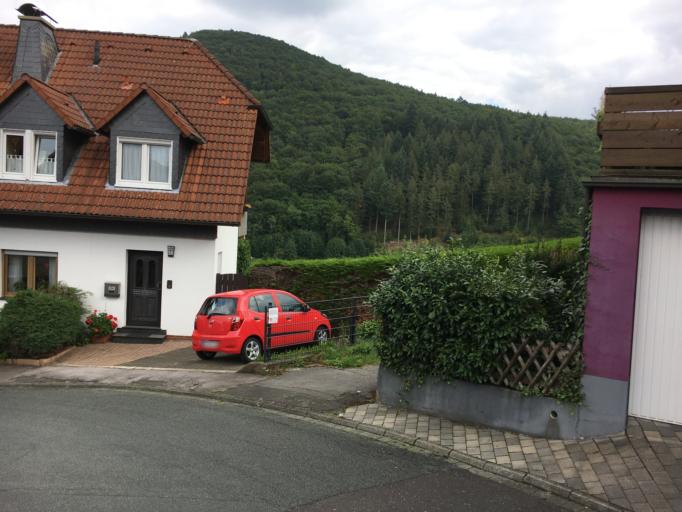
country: DE
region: North Rhine-Westphalia
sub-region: Regierungsbezirk Arnsberg
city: Lennestadt
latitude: 51.1203
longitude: 8.0660
